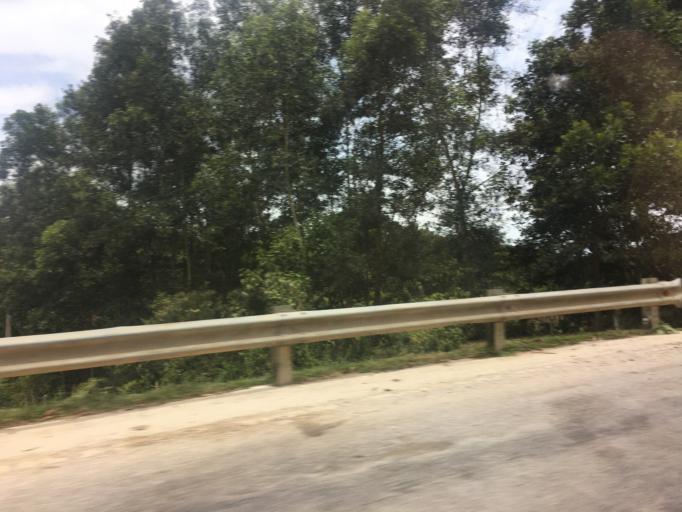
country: VN
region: Ha Tinh
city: Vu Quang
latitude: 18.3046
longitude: 105.6166
